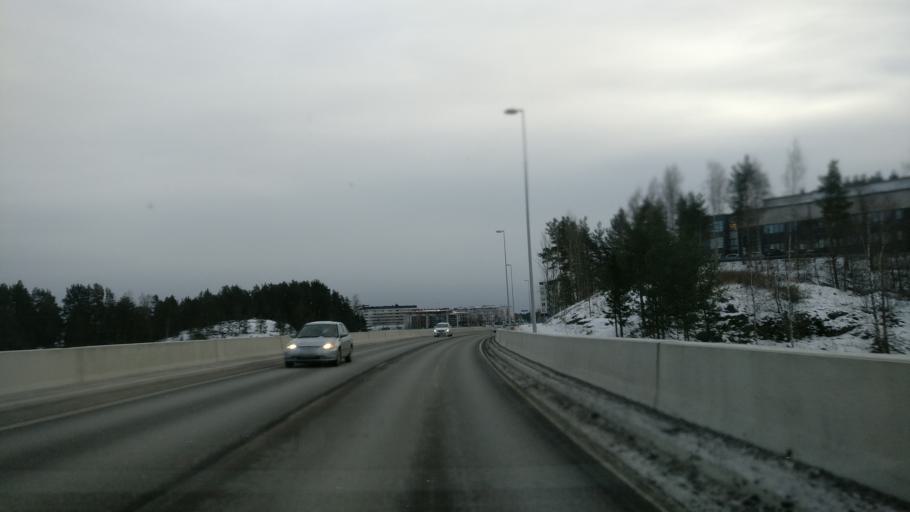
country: FI
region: Southern Savonia
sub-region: Savonlinna
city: Savonlinna
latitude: 61.8738
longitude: 28.8804
